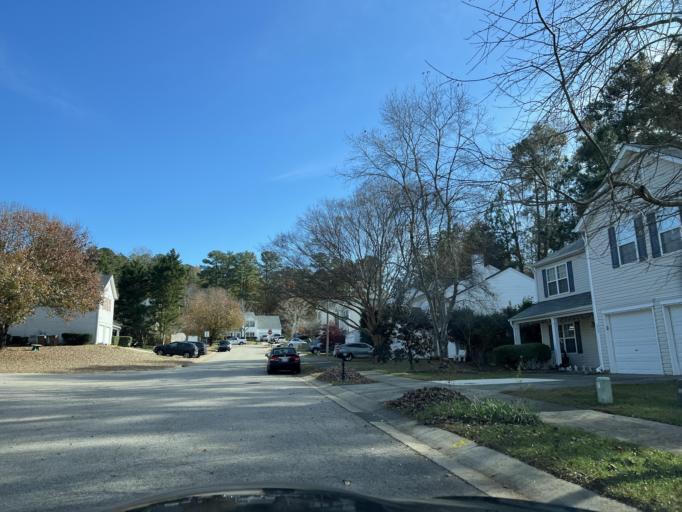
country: US
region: North Carolina
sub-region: Wake County
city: Wake Forest
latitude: 35.9647
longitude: -78.5231
